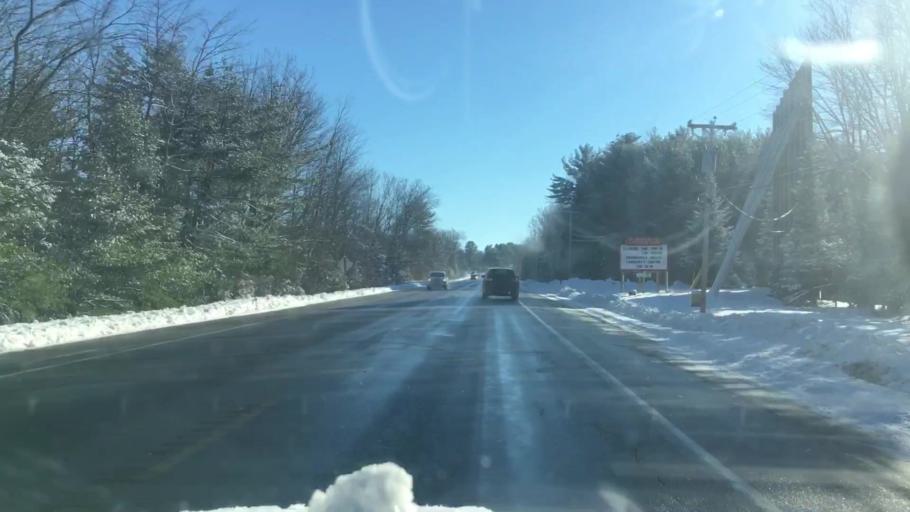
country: US
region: Maine
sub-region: Cumberland County
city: Bridgton
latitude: 44.0293
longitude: -70.6945
